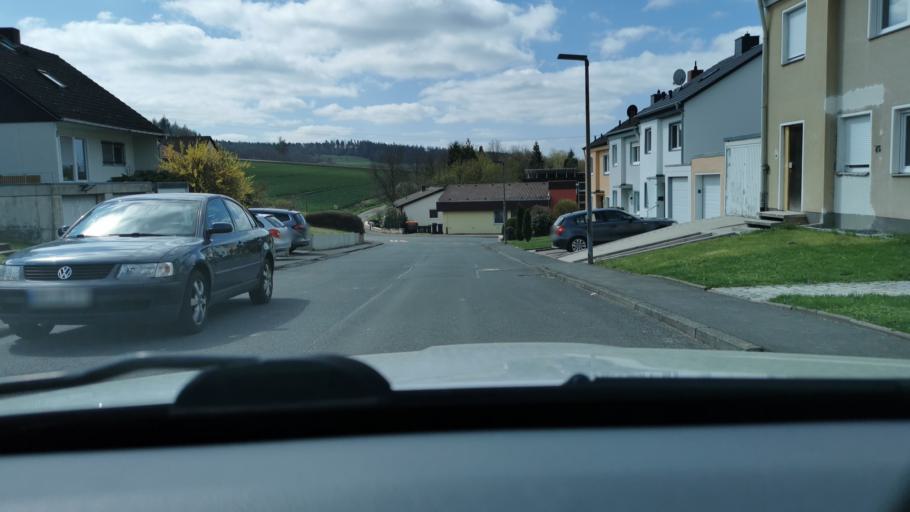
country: DE
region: Hesse
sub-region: Regierungsbezirk Kassel
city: Bad Hersfeld
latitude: 50.8610
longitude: 9.7445
